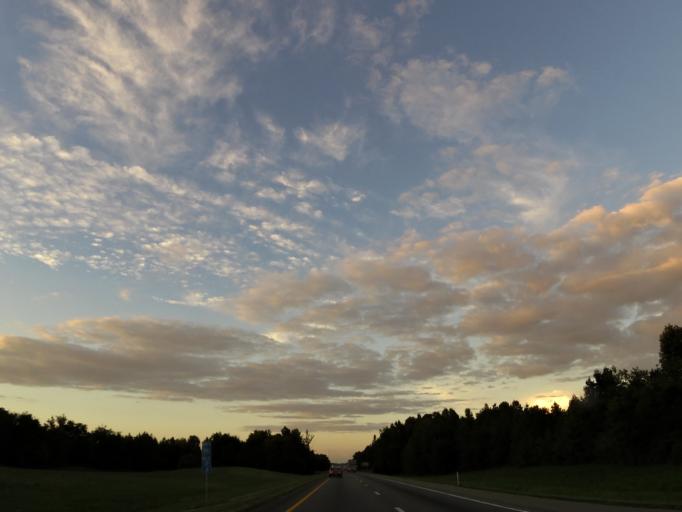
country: US
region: Tennessee
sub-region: Monroe County
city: Sweetwater
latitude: 35.5865
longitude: -84.5268
